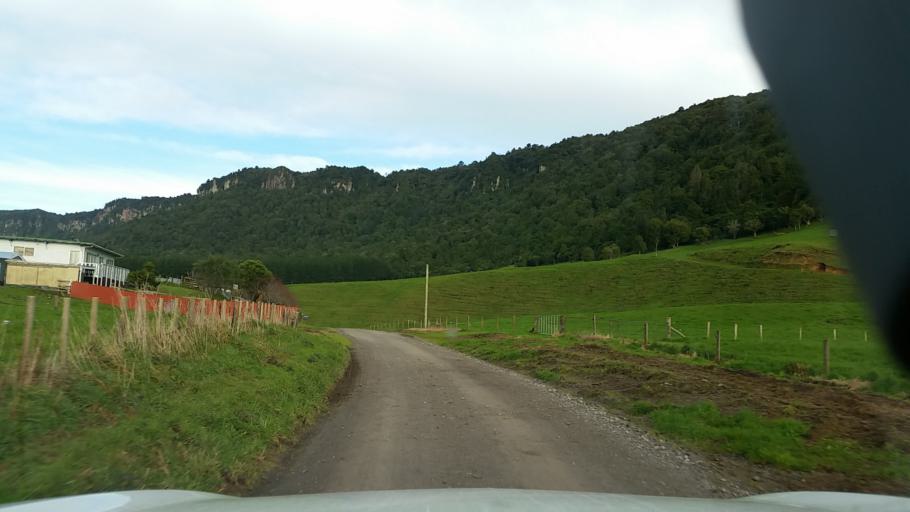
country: NZ
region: Bay of Plenty
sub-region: Rotorua District
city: Rotorua
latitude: -38.2276
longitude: 176.1618
